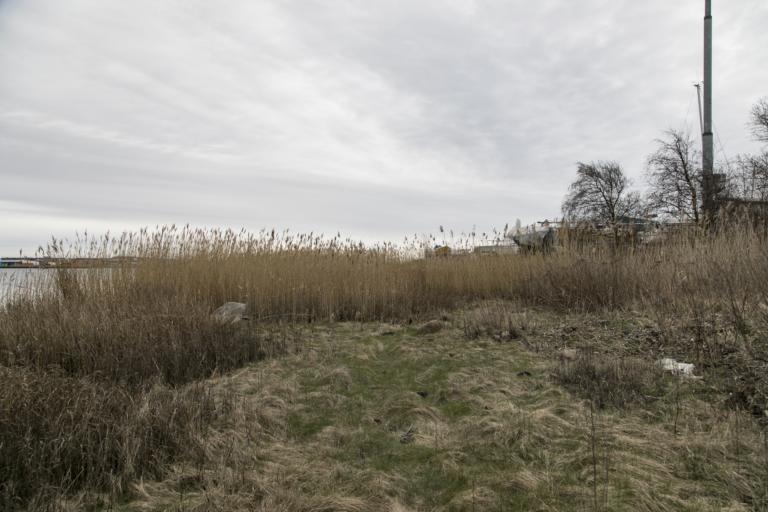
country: SE
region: Halland
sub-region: Varbergs Kommun
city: Varberg
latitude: 57.1180
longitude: 12.2273
